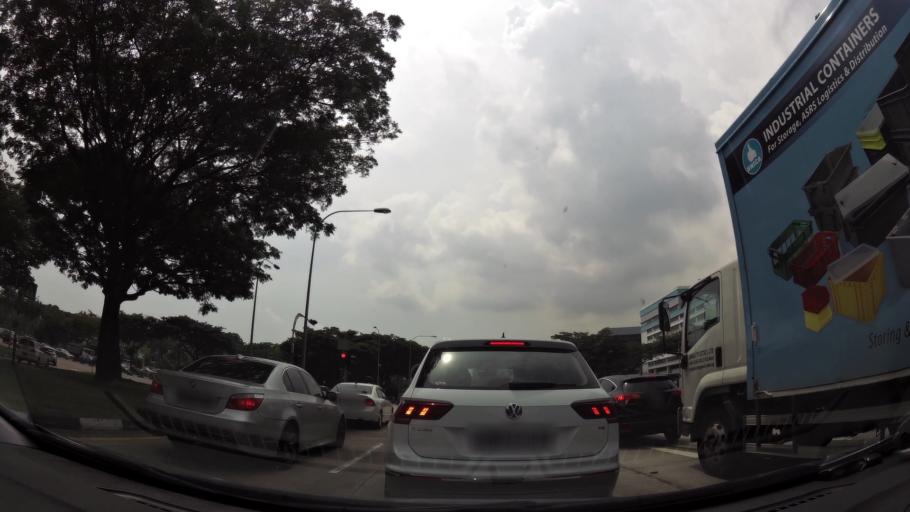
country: SG
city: Singapore
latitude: 1.3379
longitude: 103.8966
